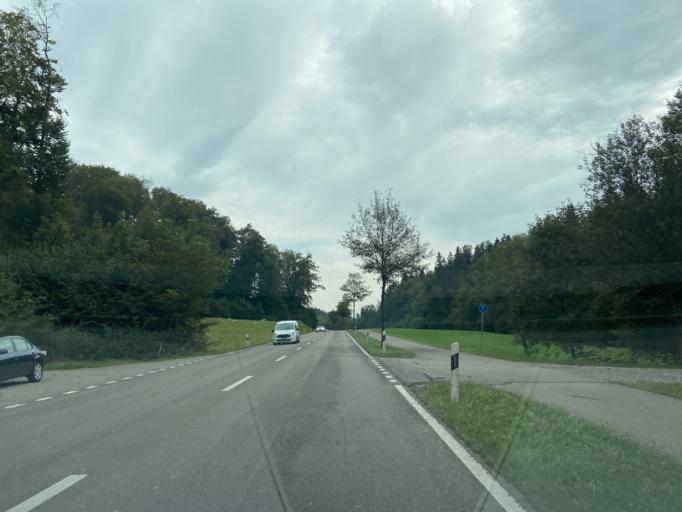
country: CH
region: Zurich
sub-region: Bezirk Pfaeffikon
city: Effretikon / Watt
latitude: 47.4254
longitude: 8.7111
